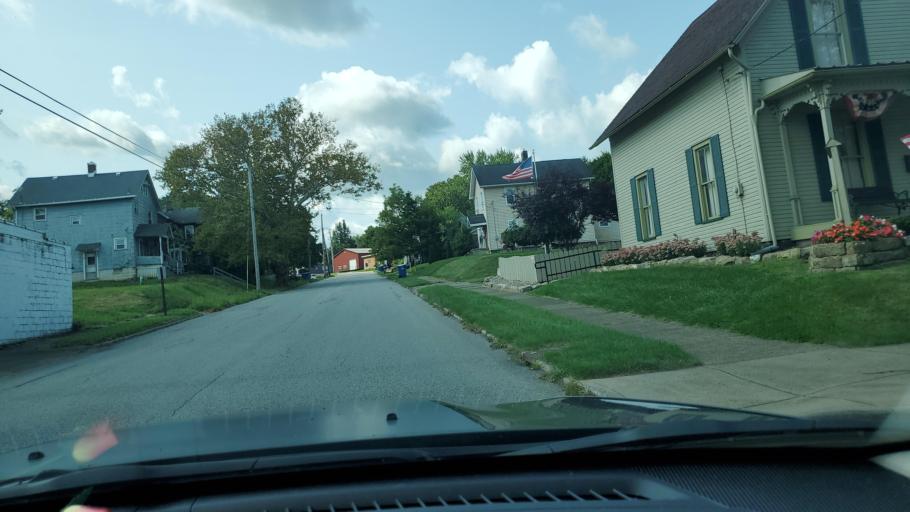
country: US
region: Ohio
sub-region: Mahoning County
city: Struthers
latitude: 41.0560
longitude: -80.5905
